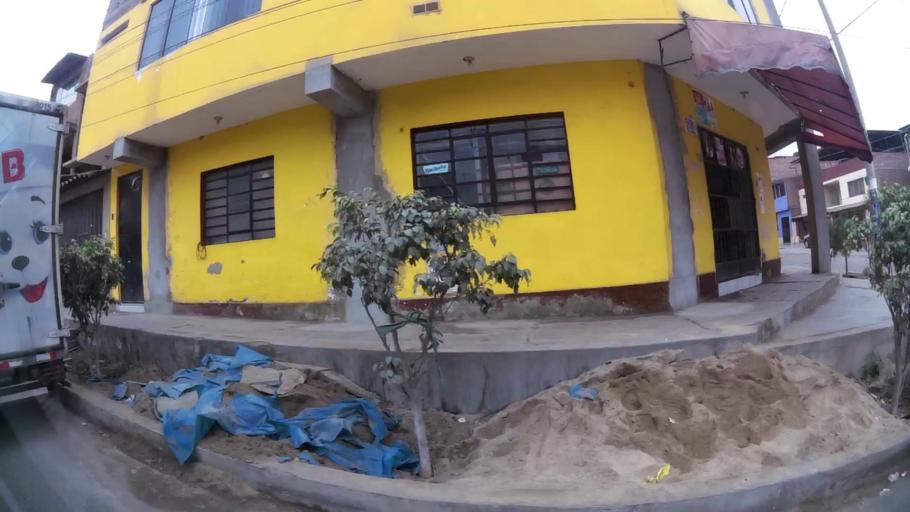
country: PE
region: Lima
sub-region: Lima
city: Surco
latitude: -12.1680
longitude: -76.9459
